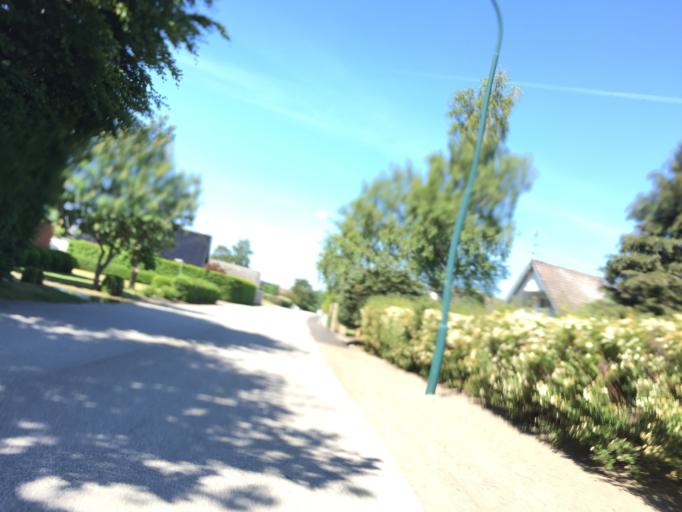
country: SE
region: Skane
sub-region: Trelleborgs Kommun
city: Trelleborg
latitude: 55.3554
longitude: 13.2412
